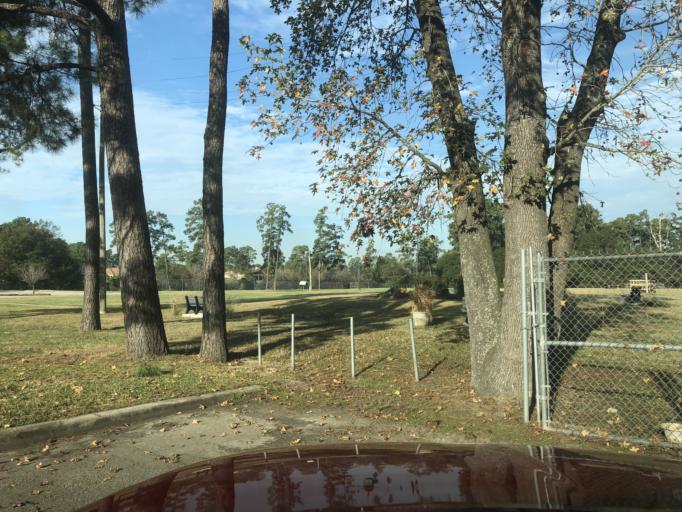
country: US
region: Texas
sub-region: Harris County
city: Spring
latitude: 30.0064
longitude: -95.4714
